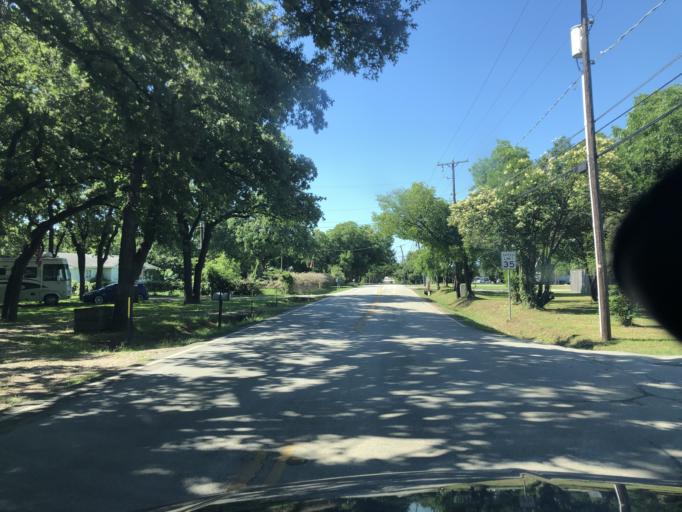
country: US
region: Texas
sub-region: Dallas County
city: Grand Prairie
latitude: 32.8081
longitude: -97.0203
